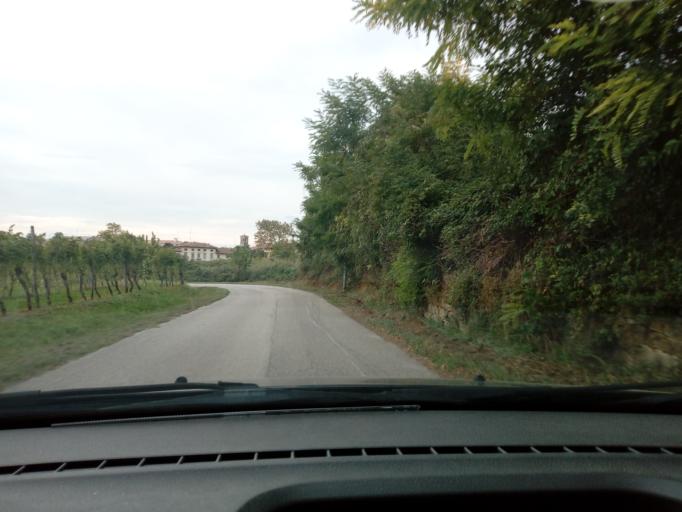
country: IT
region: Friuli Venezia Giulia
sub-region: Provincia di Udine
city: Cividale del Friuli
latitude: 46.0835
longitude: 13.4382
